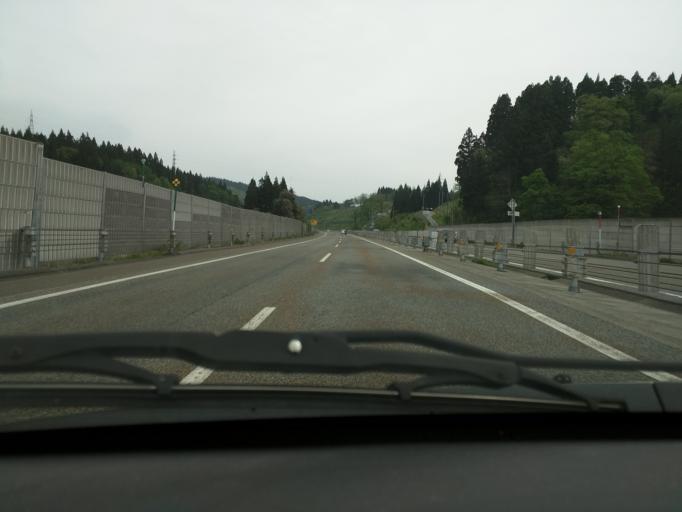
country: JP
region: Niigata
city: Ojiya
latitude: 37.2837
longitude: 138.7865
